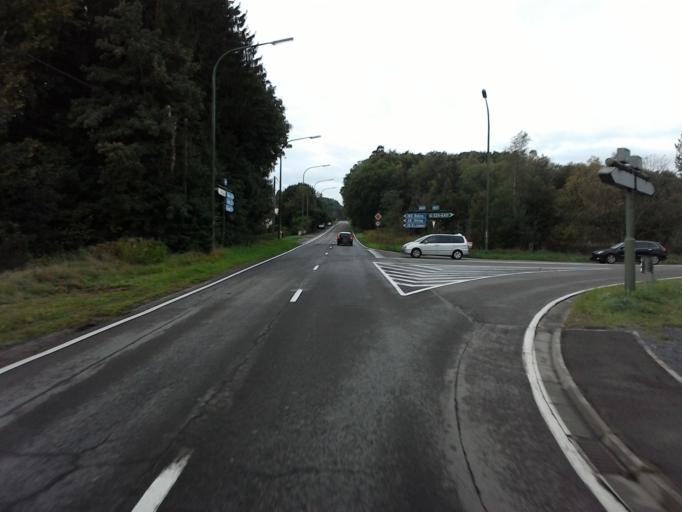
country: BE
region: Wallonia
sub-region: Province du Luxembourg
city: Arlon
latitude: 49.6736
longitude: 5.7905
